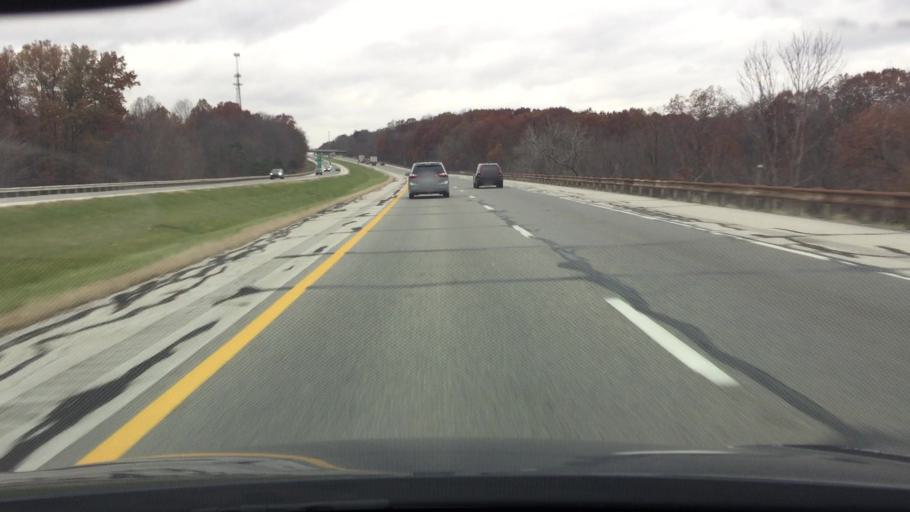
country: US
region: Ohio
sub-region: Mahoning County
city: Canfield
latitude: 41.0276
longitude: -80.7274
